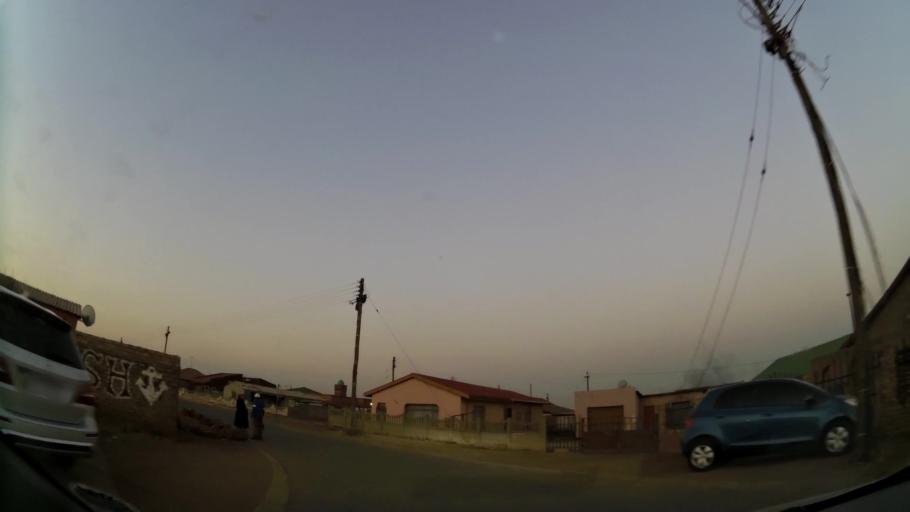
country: ZA
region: Gauteng
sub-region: West Rand District Municipality
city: Randfontein
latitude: -26.2062
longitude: 27.7130
